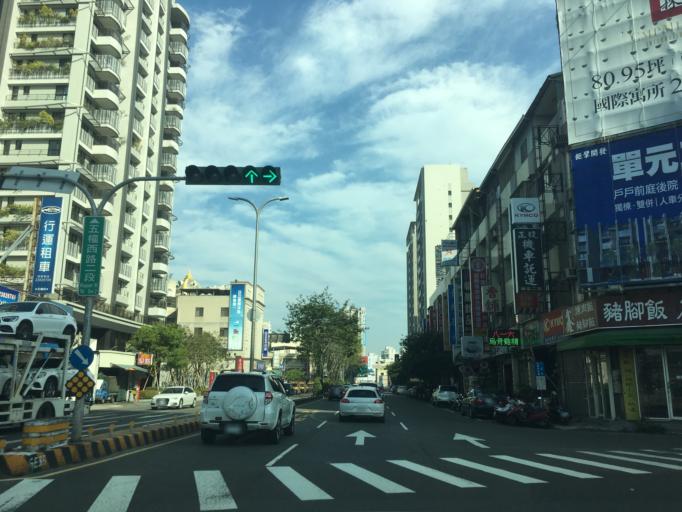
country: TW
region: Taiwan
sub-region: Taichung City
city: Taichung
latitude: 24.1443
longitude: 120.6342
